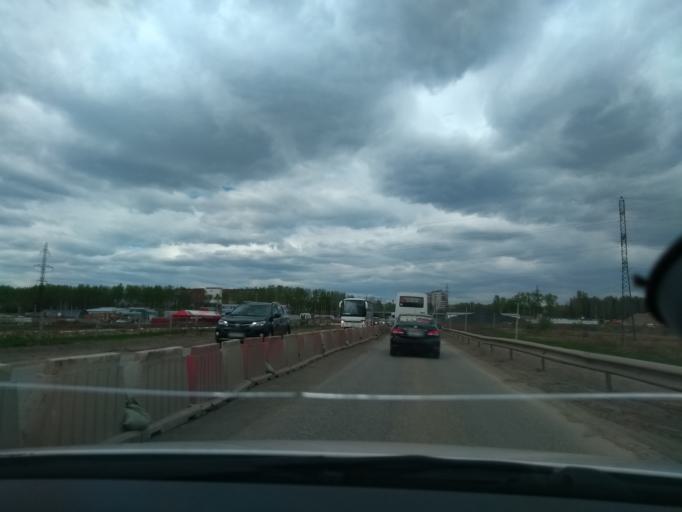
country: RU
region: Perm
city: Froly
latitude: 57.9385
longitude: 56.2690
